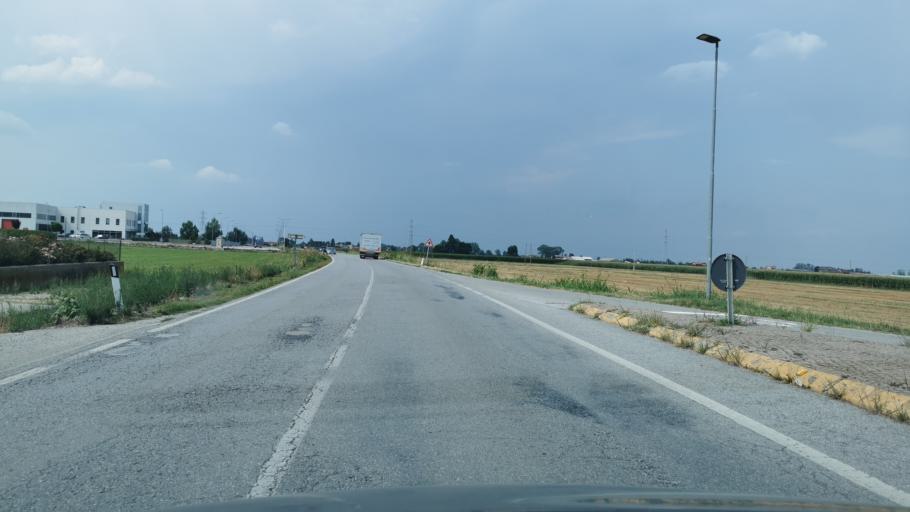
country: IT
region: Piedmont
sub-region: Provincia di Cuneo
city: Tarantasca
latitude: 44.5010
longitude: 7.5420
